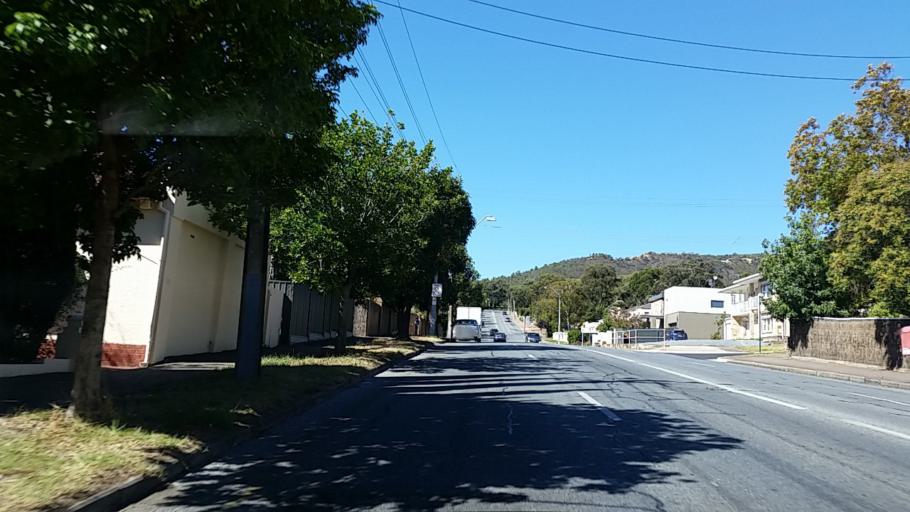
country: AU
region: South Australia
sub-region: Burnside
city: Hazelwood Park
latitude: -34.9380
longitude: 138.6650
